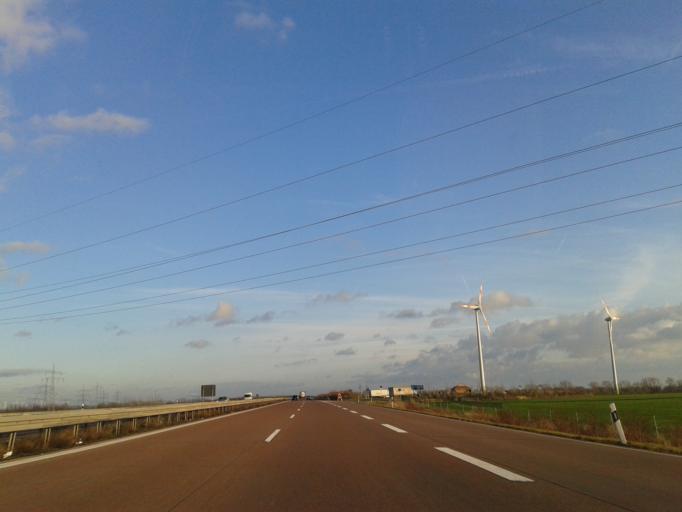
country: DE
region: Saxony-Anhalt
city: Stedten
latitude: 51.4005
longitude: 11.7218
